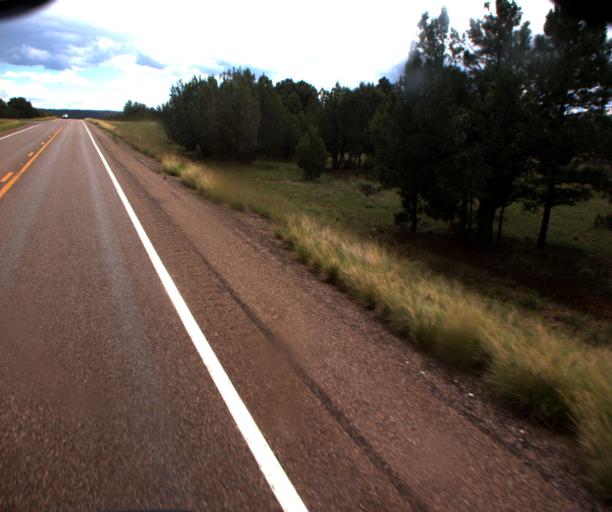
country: US
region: Arizona
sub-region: Navajo County
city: Linden
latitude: 34.3592
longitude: -110.3217
